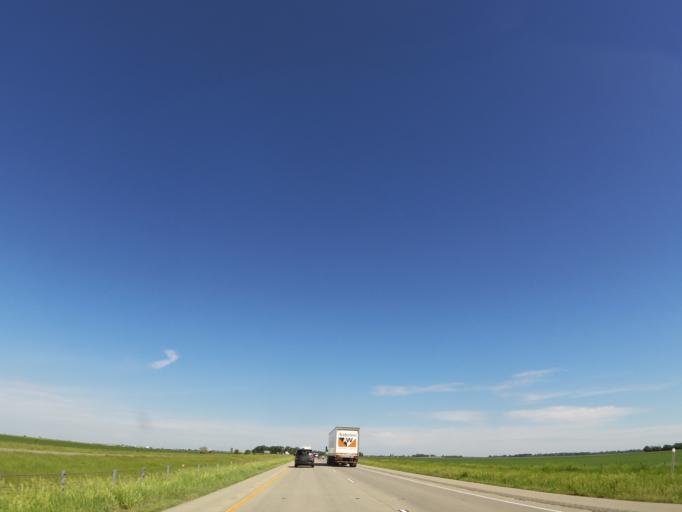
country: US
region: Minnesota
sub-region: Clay County
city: Glyndon
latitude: 46.8371
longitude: -96.6247
